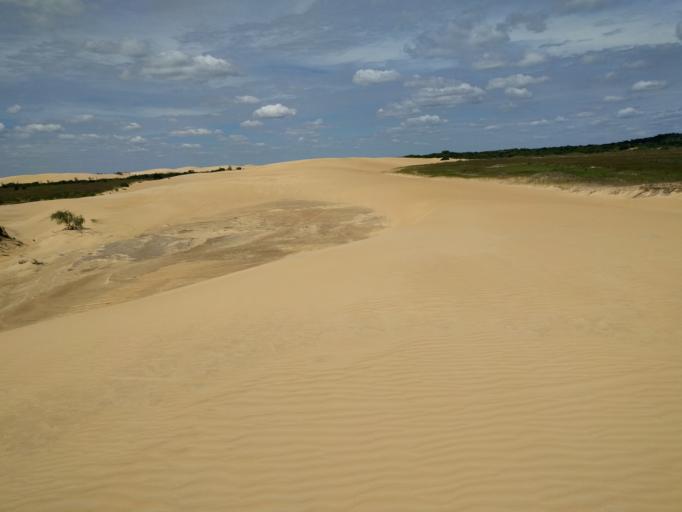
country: BO
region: Santa Cruz
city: Santa Cruz de la Sierra
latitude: -17.9460
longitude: -63.1599
